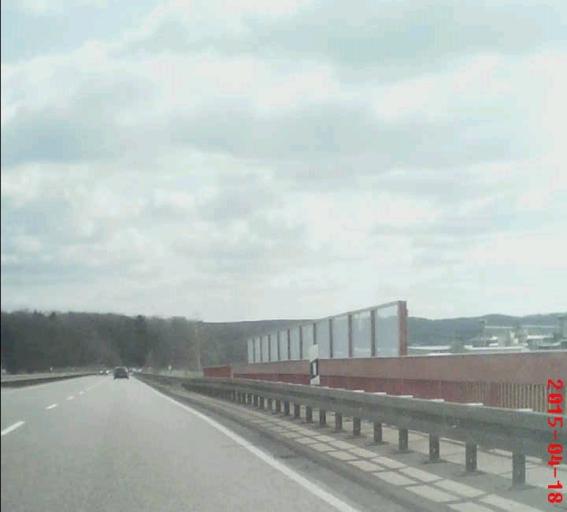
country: DE
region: Thuringia
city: Hausen
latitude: 51.3859
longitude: 10.3466
